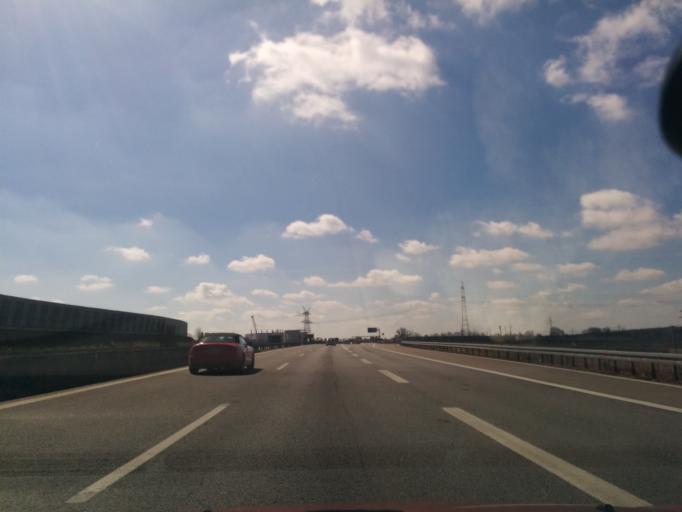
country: DE
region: Bavaria
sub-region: Upper Bavaria
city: Karlsfeld
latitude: 48.1843
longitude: 11.4348
